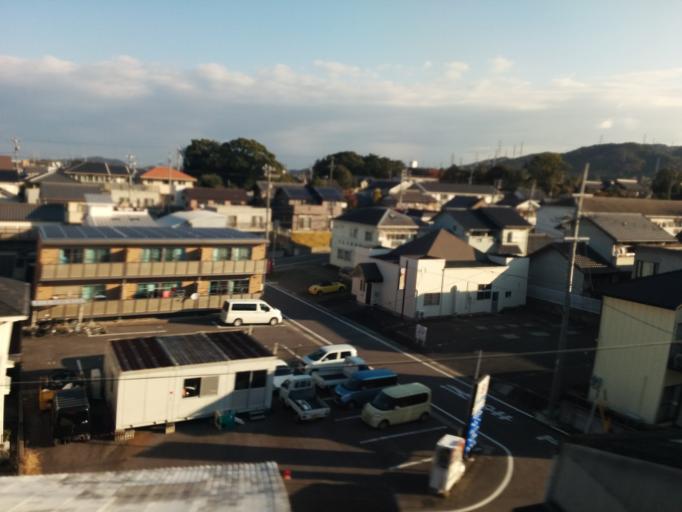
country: JP
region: Aichi
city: Gamagori
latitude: 34.8569
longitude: 137.1665
